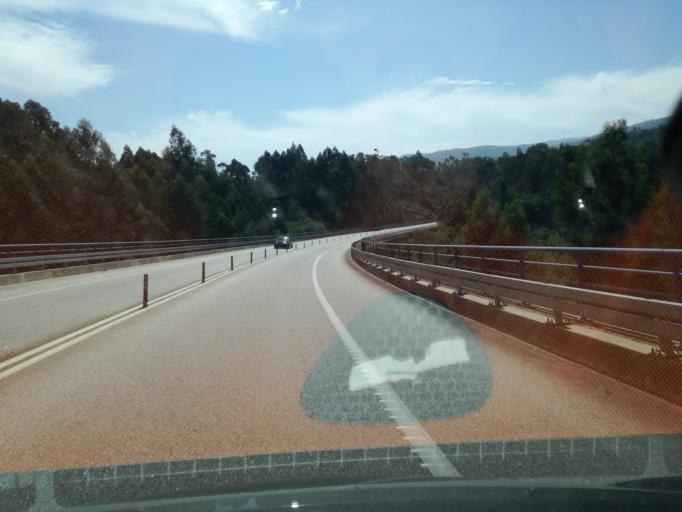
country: PT
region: Viana do Castelo
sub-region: Vila Nova de Cerveira
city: Vila Nova de Cerveira
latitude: 41.8965
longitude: -8.7745
